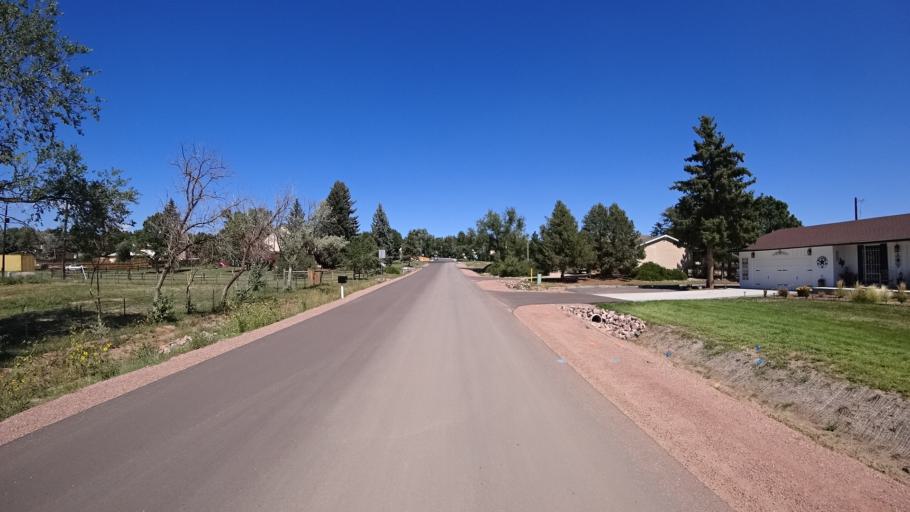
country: US
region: Colorado
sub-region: El Paso County
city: Cimarron Hills
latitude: 38.8667
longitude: -104.7294
